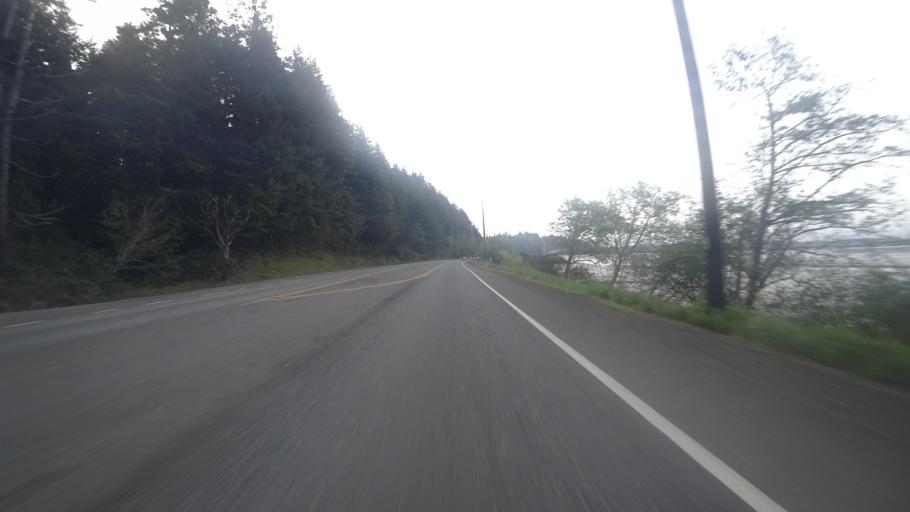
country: US
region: Oregon
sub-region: Coos County
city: North Bend
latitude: 43.4529
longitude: -124.2272
